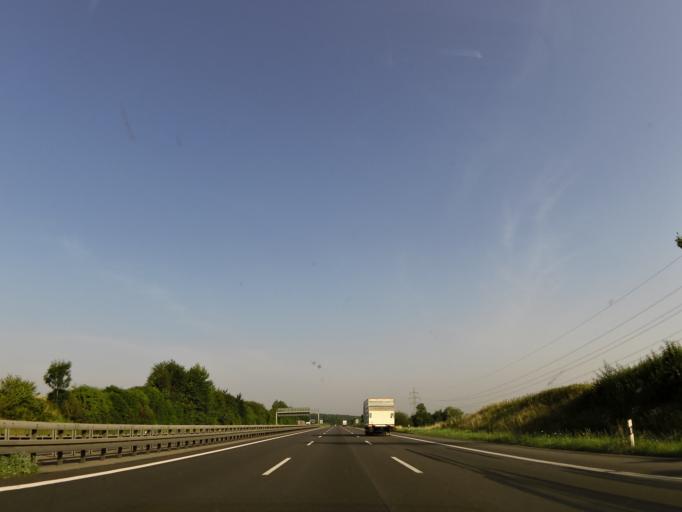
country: DE
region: Baden-Wuerttemberg
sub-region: Regierungsbezirk Stuttgart
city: Kirchheim unter Teck
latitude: 48.6436
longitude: 9.4266
